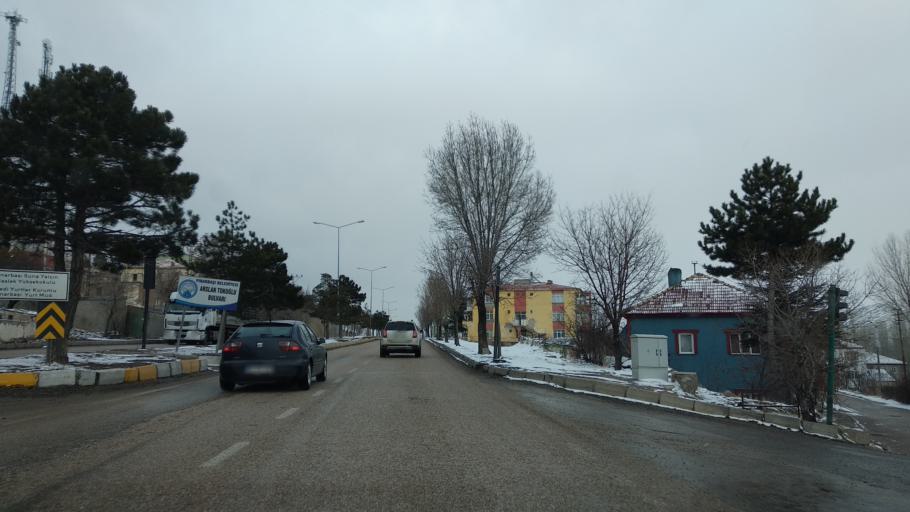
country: TR
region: Kayseri
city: Pinarbasi
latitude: 38.7232
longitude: 36.3903
